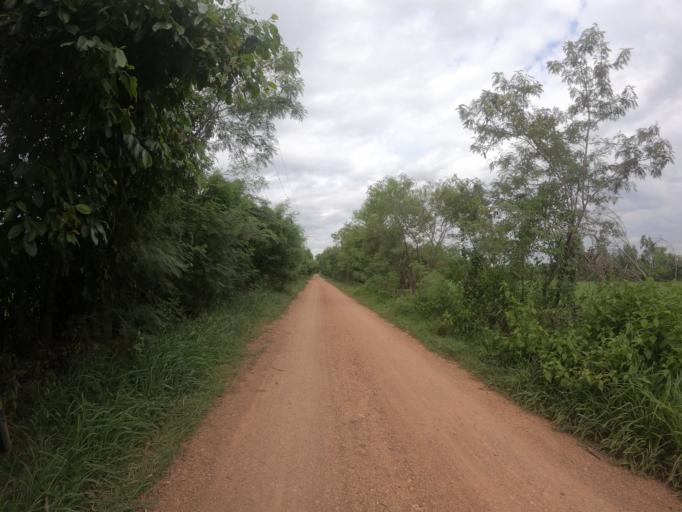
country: TH
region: Pathum Thani
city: Nong Suea
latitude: 14.0762
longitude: 100.8416
